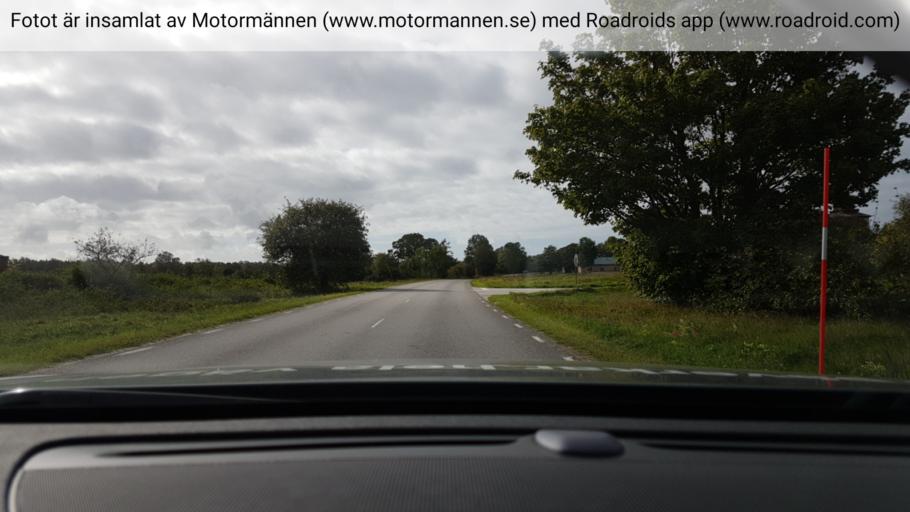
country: SE
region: Gotland
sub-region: Gotland
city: Hemse
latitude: 56.9720
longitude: 18.2347
